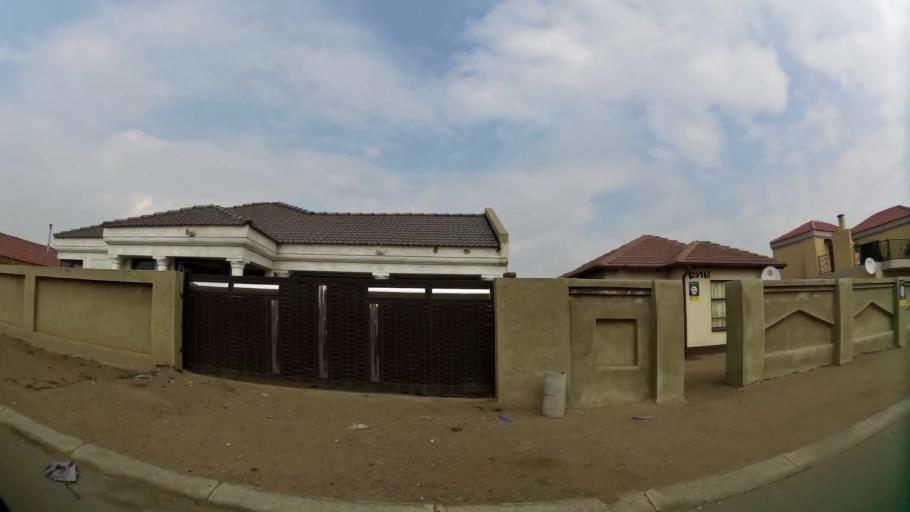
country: ZA
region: Gauteng
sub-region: Sedibeng District Municipality
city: Vanderbijlpark
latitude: -26.6853
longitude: 27.8432
